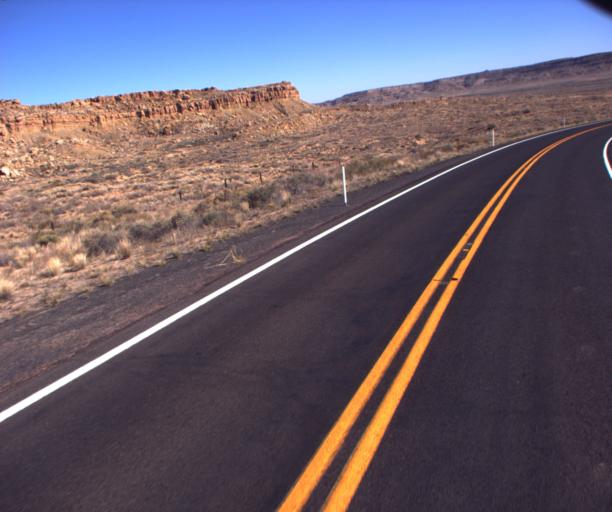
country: US
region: Arizona
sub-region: Navajo County
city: First Mesa
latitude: 35.8833
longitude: -110.6210
